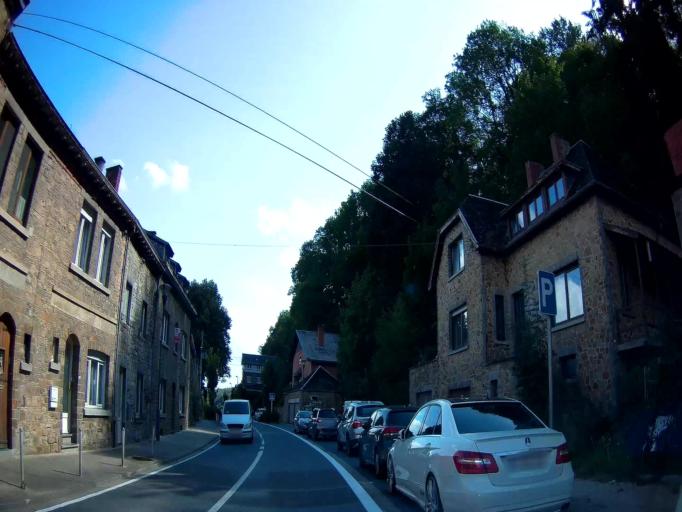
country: BE
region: Wallonia
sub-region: Province de Namur
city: Profondeville
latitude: 50.3460
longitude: 4.8532
